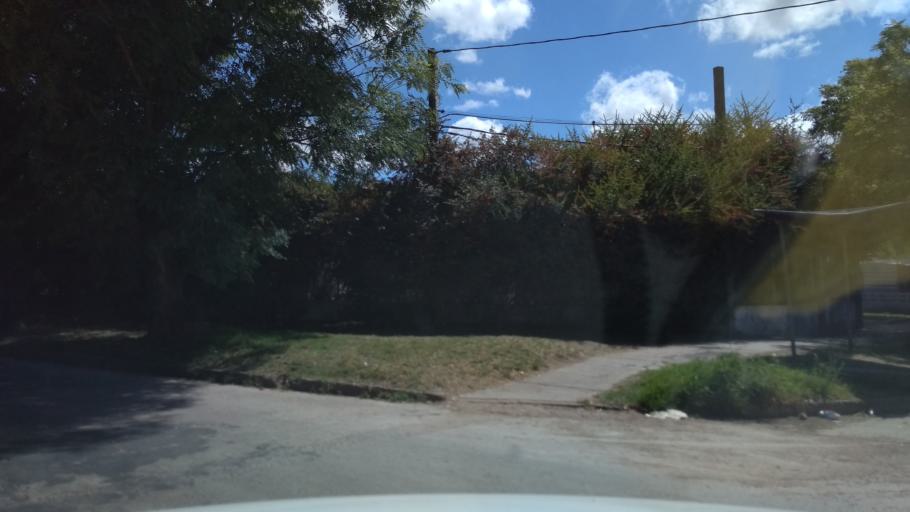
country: UY
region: Canelones
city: La Paz
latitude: -34.8282
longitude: -56.2258
